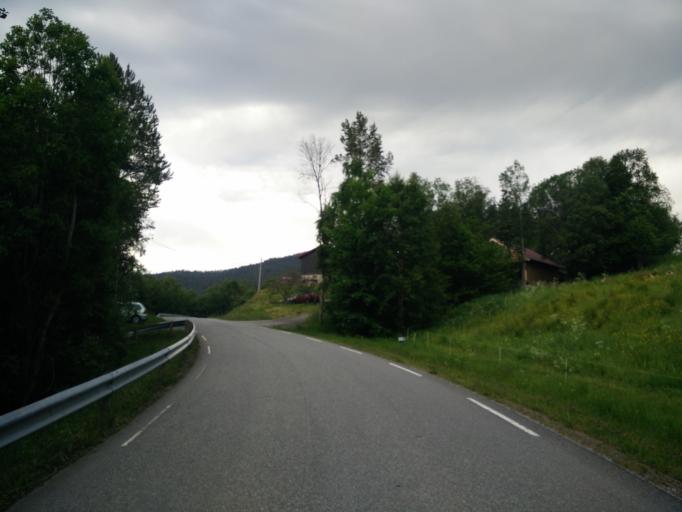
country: NO
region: More og Romsdal
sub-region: Kristiansund
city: Rensvik
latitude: 63.0239
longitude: 7.9524
